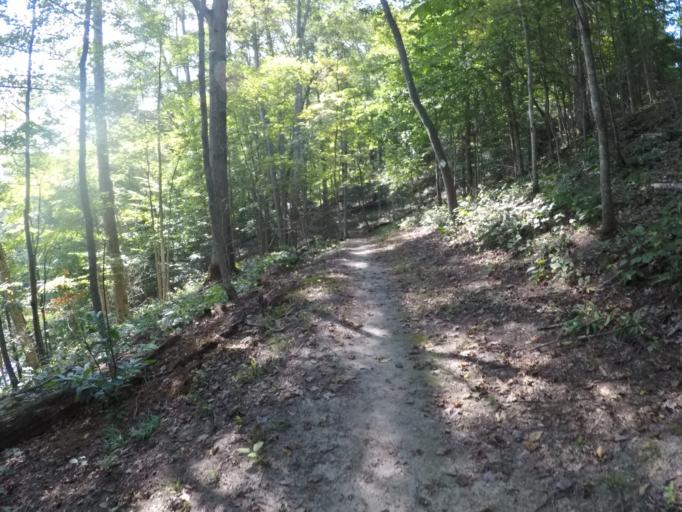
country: US
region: Ohio
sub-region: Lawrence County
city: Ironton
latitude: 38.6171
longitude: -82.6256
